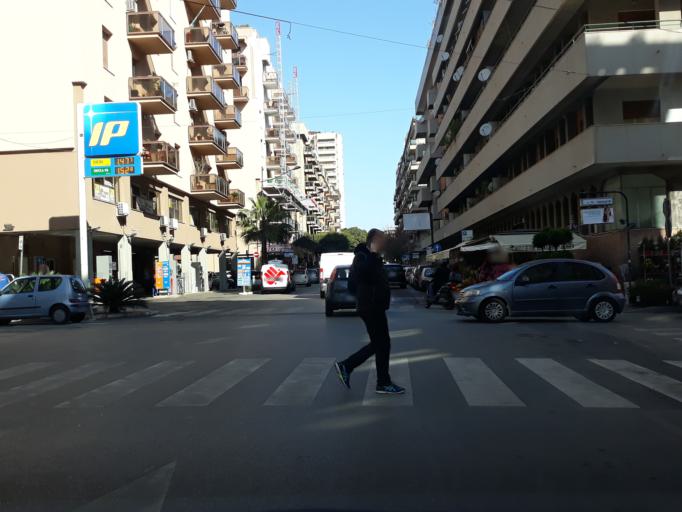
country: IT
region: Sicily
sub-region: Palermo
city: Palermo
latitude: 38.1347
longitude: 13.3456
